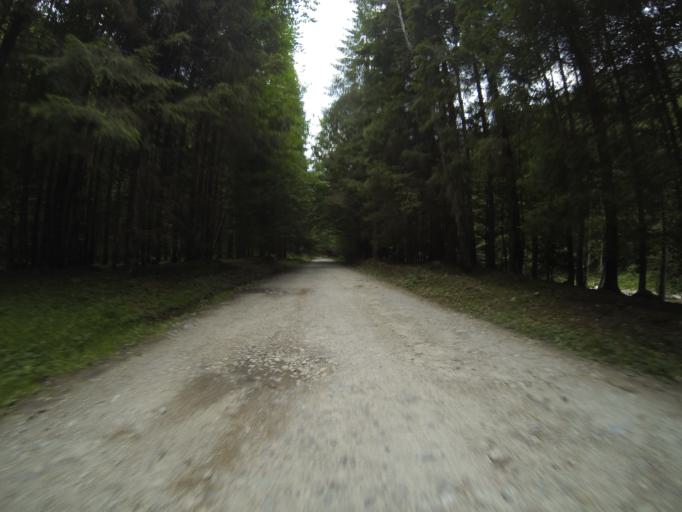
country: RO
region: Gorj
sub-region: Comuna Polovragi
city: Polovragi
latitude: 45.2534
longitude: 23.7667
